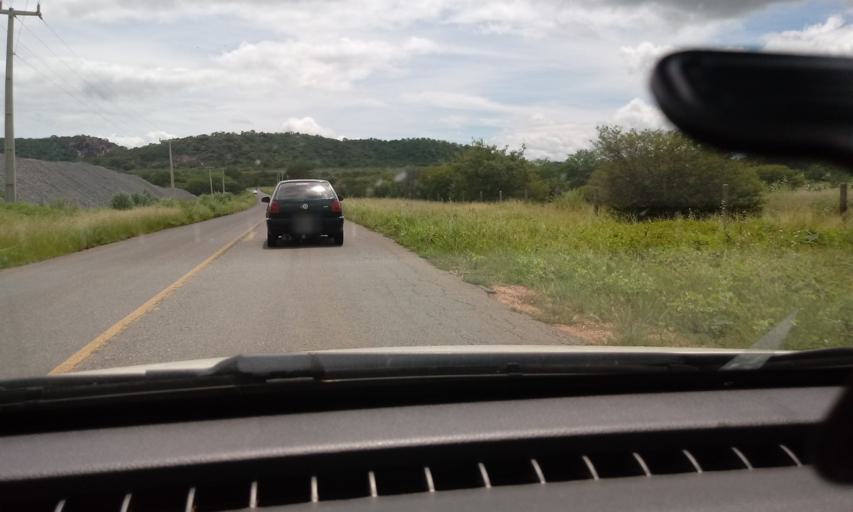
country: BR
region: Bahia
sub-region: Guanambi
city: Guanambi
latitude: -14.1471
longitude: -42.8365
